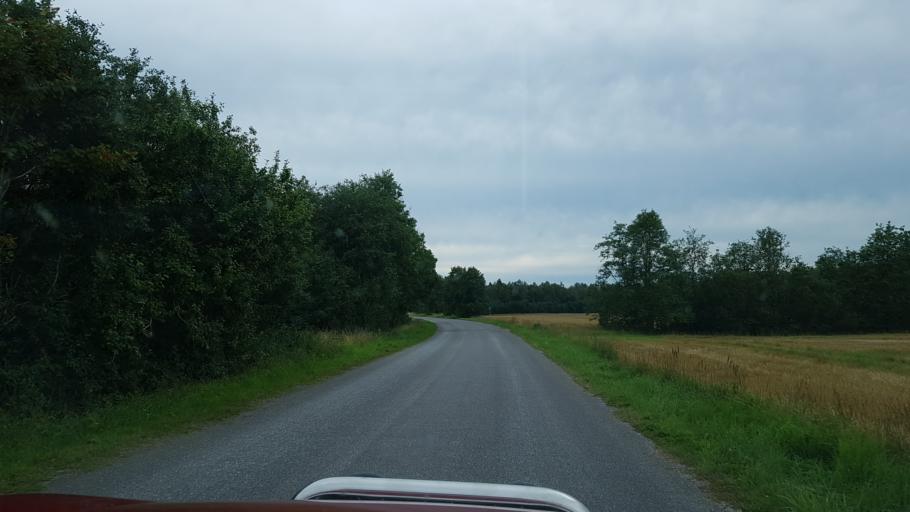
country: EE
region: Laeaene
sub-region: Lihula vald
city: Lihula
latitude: 58.8370
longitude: 23.8125
